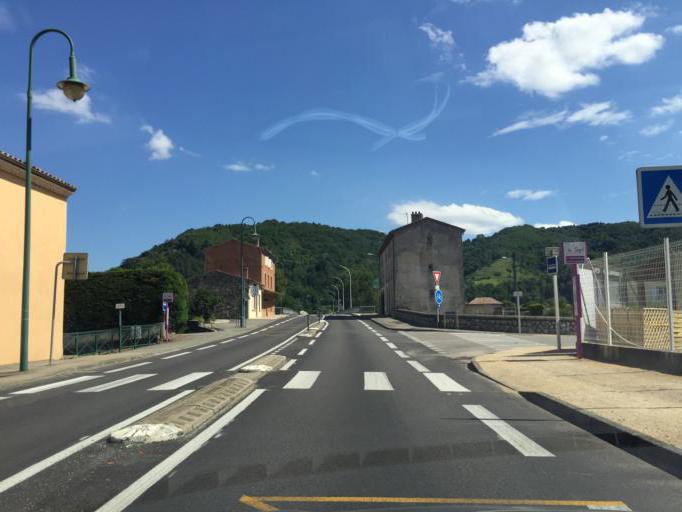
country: FR
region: Rhone-Alpes
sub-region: Departement de l'Ardeche
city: Saint-Jean-de-Muzols
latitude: 45.0760
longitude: 4.8160
